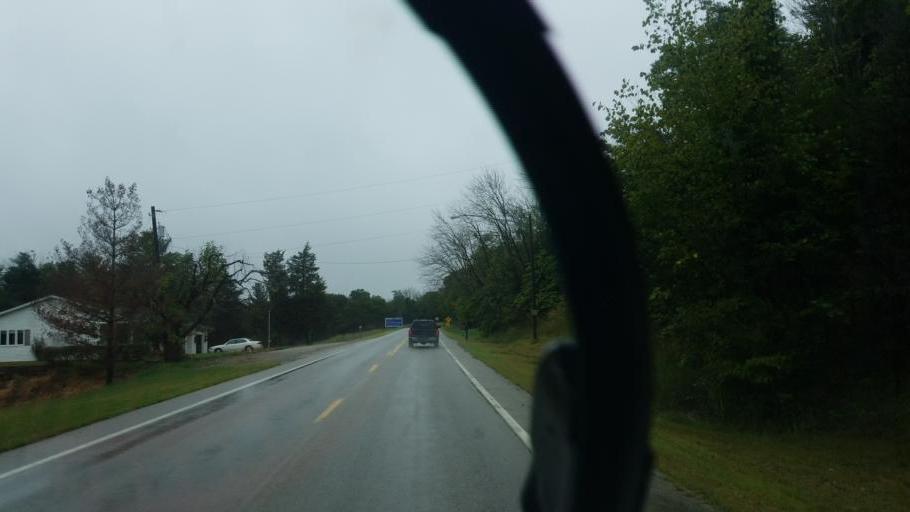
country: US
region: Ohio
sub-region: Adams County
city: West Union
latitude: 38.7956
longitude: -83.5221
